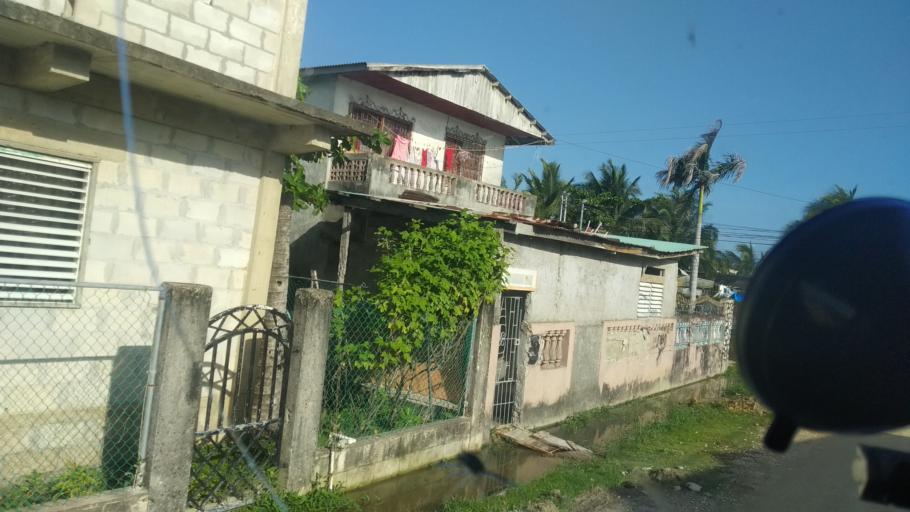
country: BZ
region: Belize
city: Belize City
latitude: 17.4851
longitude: -88.2048
